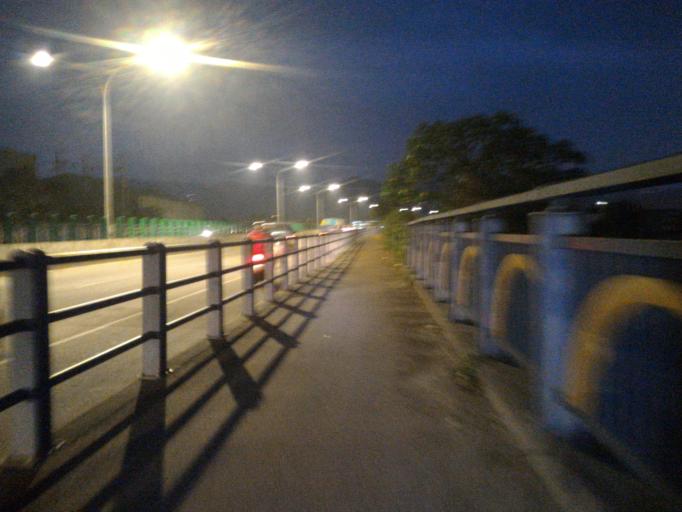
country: TW
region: Taipei
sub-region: Taipei
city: Banqiao
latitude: 24.9624
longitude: 121.4058
